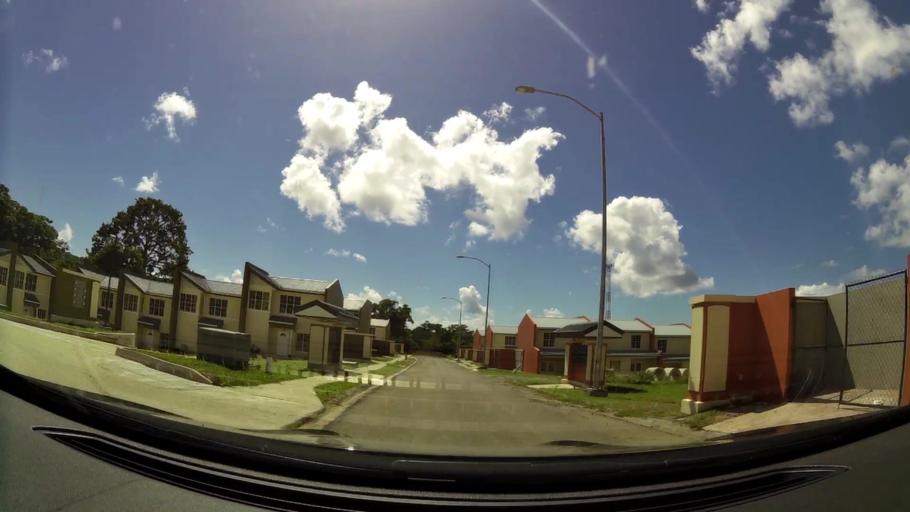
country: TT
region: Tobago
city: Scarborough
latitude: 11.2197
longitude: -60.7712
